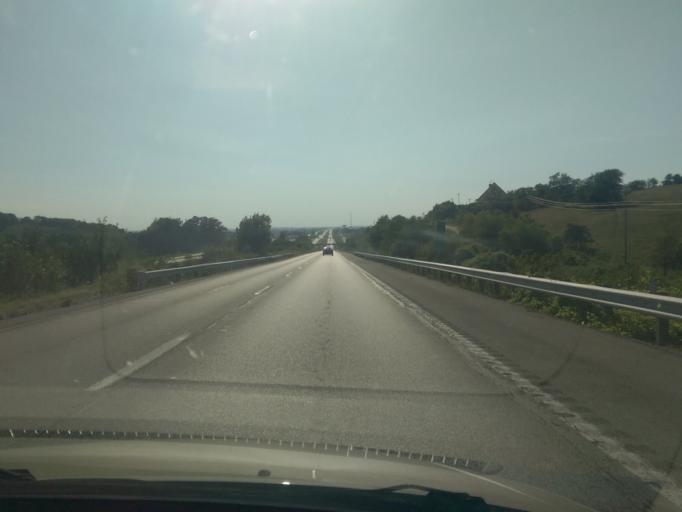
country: US
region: Missouri
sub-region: Lafayette County
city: Odessa
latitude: 39.0084
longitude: -93.9565
